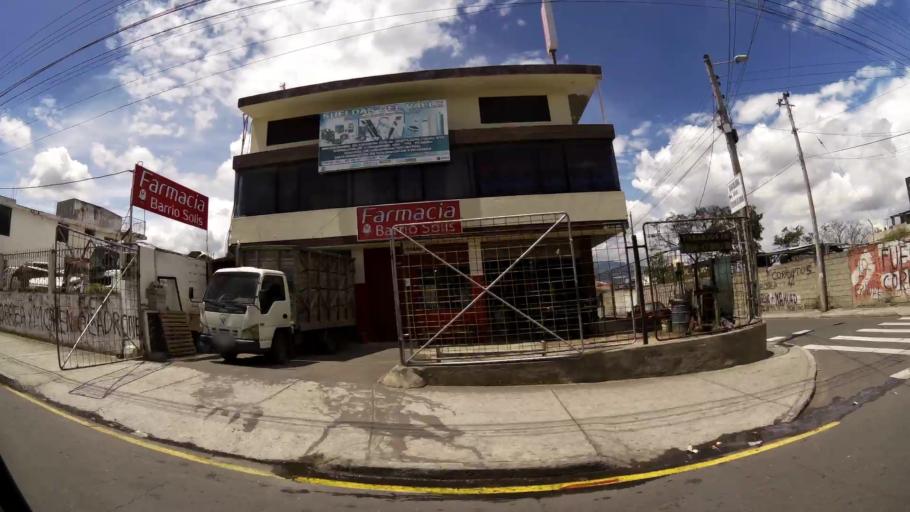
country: EC
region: Tungurahua
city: Ambato
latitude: -1.2760
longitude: -78.6235
